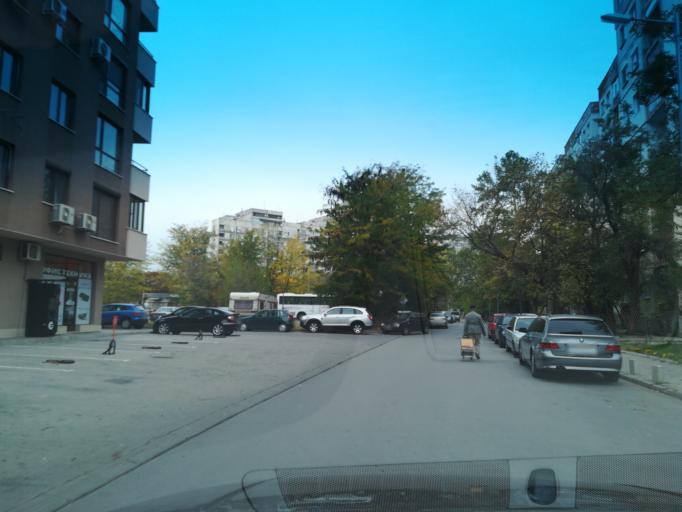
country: BG
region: Plovdiv
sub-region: Obshtina Plovdiv
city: Plovdiv
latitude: 42.1383
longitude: 24.7933
